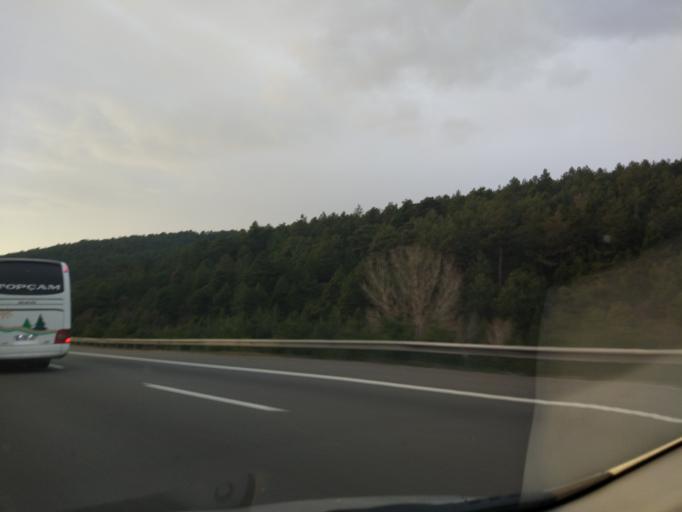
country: TR
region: Bolu
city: Gokcesu
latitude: 40.7395
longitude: 31.8285
